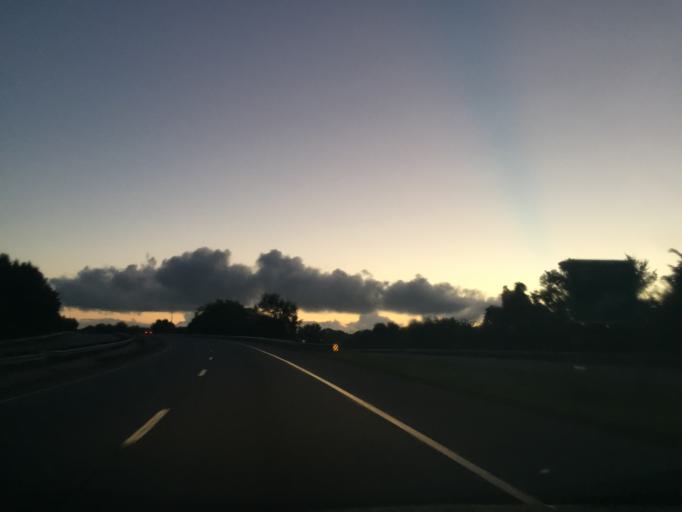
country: US
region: Georgia
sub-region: Chatham County
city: Thunderbolt
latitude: 32.0406
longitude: -81.0714
